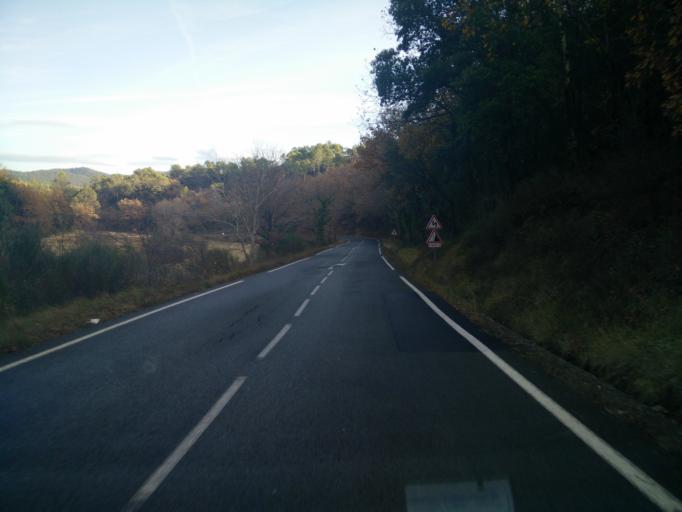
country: FR
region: Provence-Alpes-Cote d'Azur
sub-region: Departement du Var
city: Meounes-les-Montrieux
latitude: 43.2795
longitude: 5.9465
